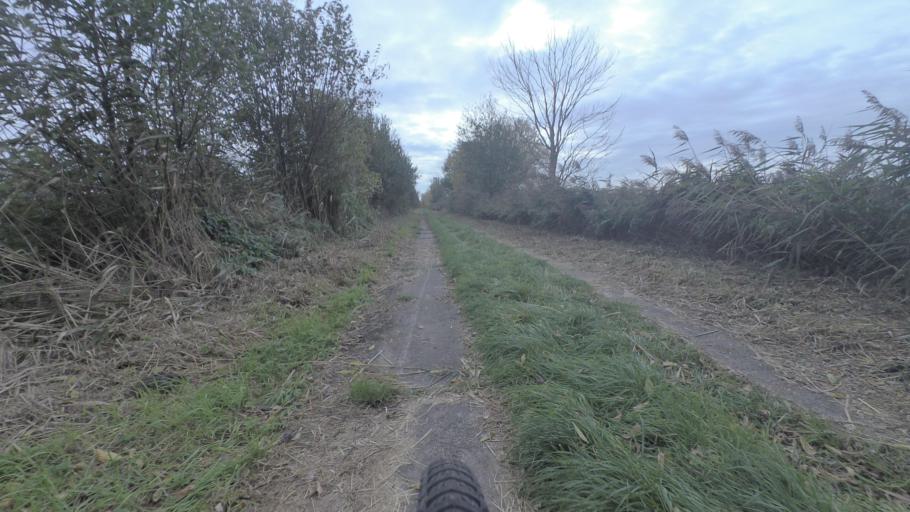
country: DE
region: Brandenburg
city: Grossbeeren
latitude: 52.3010
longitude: 13.3350
